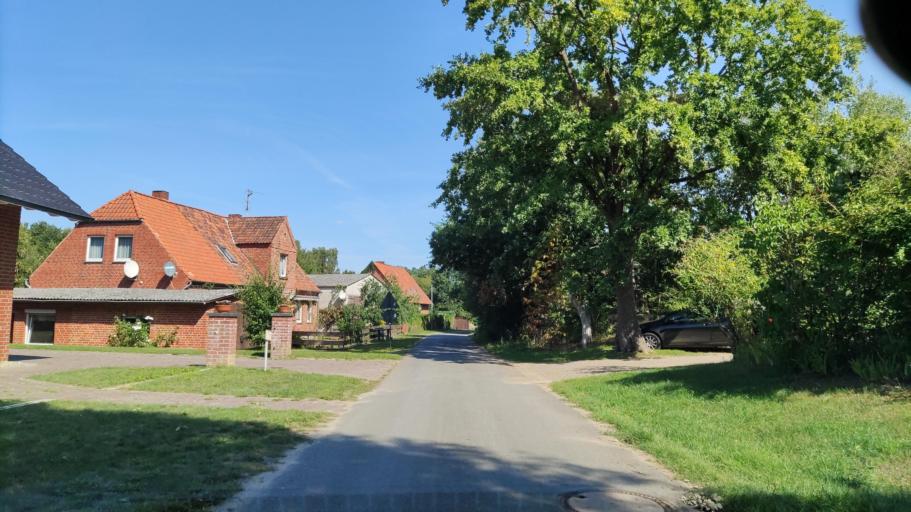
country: DE
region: Lower Saxony
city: Hitzacker
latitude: 53.1468
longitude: 10.9810
